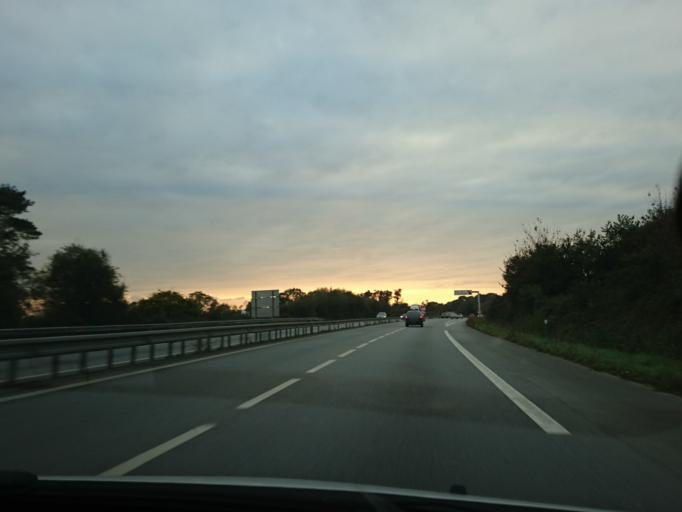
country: FR
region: Brittany
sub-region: Departement du Morbihan
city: Pluneret
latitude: 47.6613
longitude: -2.9663
